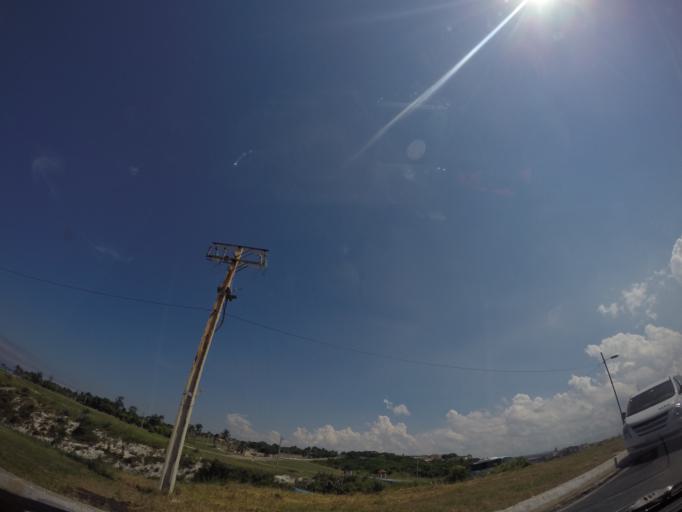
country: CU
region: La Habana
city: Centro Habana
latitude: 23.1506
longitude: -82.3552
